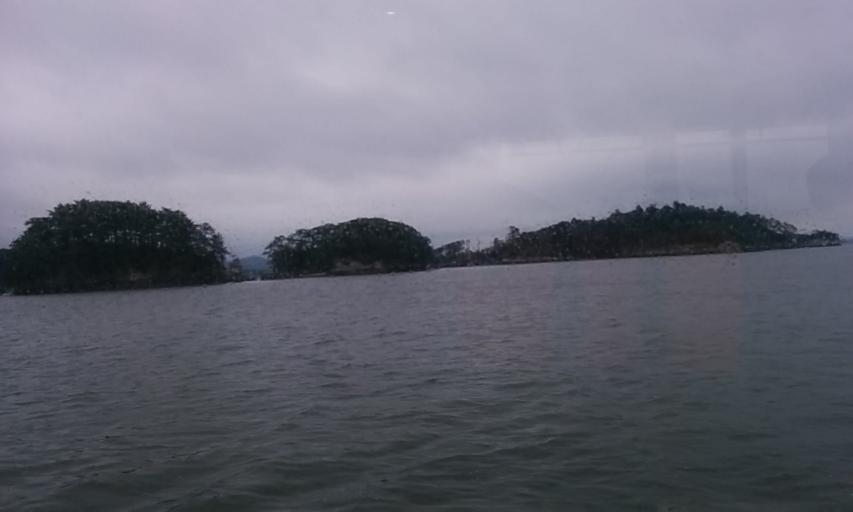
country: JP
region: Miyagi
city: Matsushima
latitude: 38.3611
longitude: 141.0697
